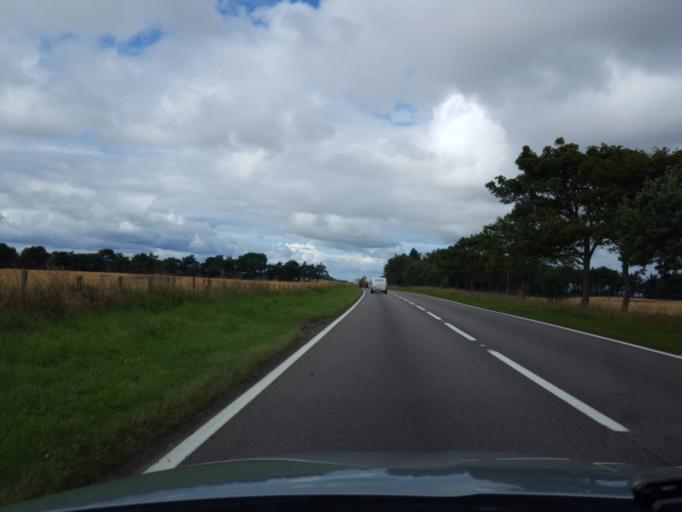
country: GB
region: Scotland
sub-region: Moray
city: Kinloss
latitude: 57.6250
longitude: -3.5288
